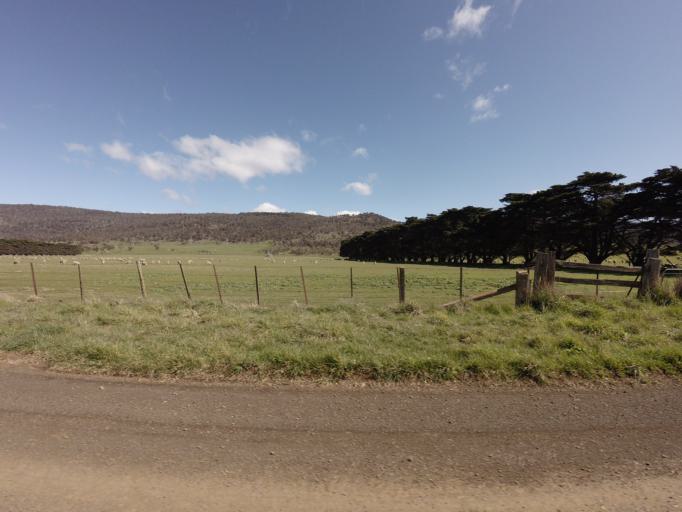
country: AU
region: Tasmania
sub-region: Northern Midlands
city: Evandale
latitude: -41.9549
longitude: 147.4361
